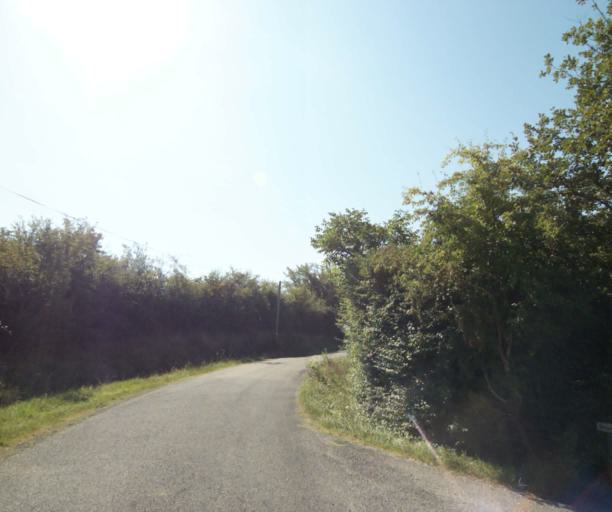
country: FR
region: Midi-Pyrenees
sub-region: Departement de l'Ariege
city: Lezat-sur-Leze
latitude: 43.2490
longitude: 1.3736
